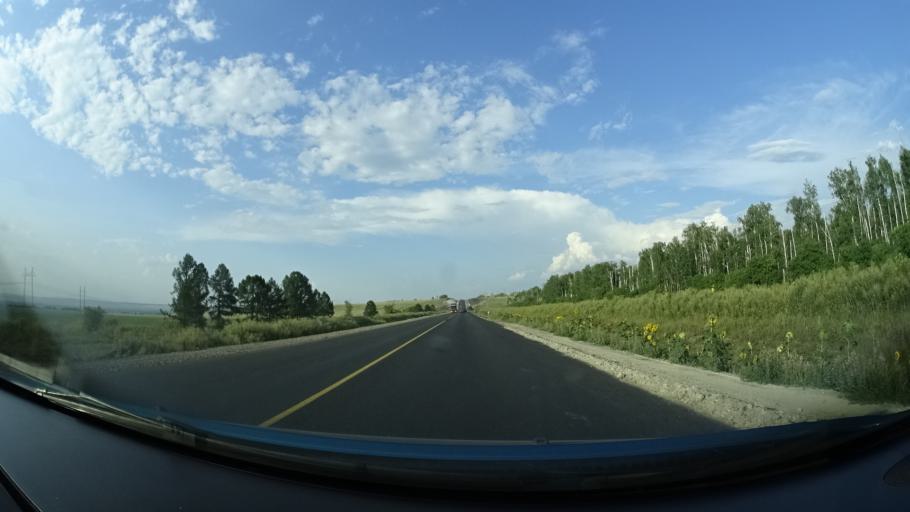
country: RU
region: Samara
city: Sukhodol
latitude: 53.7256
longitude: 50.8340
